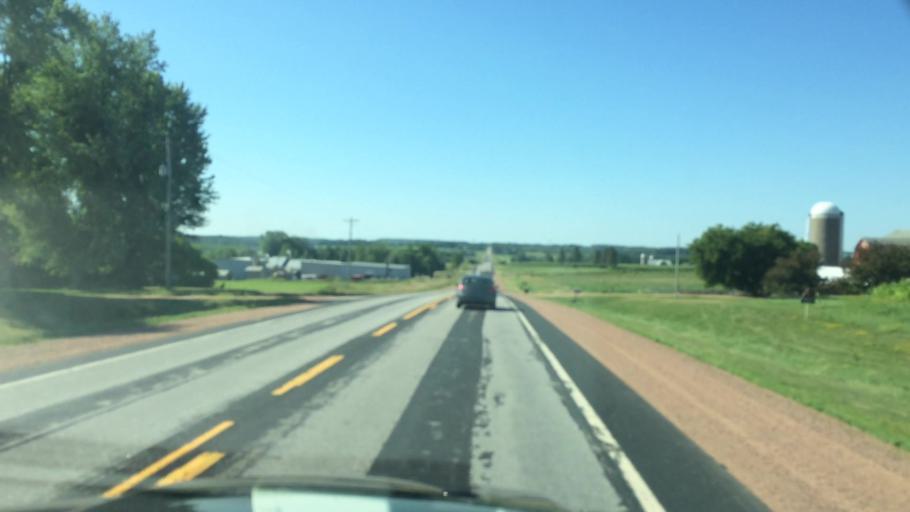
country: US
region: Wisconsin
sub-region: Marathon County
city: Stratford
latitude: 44.8336
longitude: -90.0792
